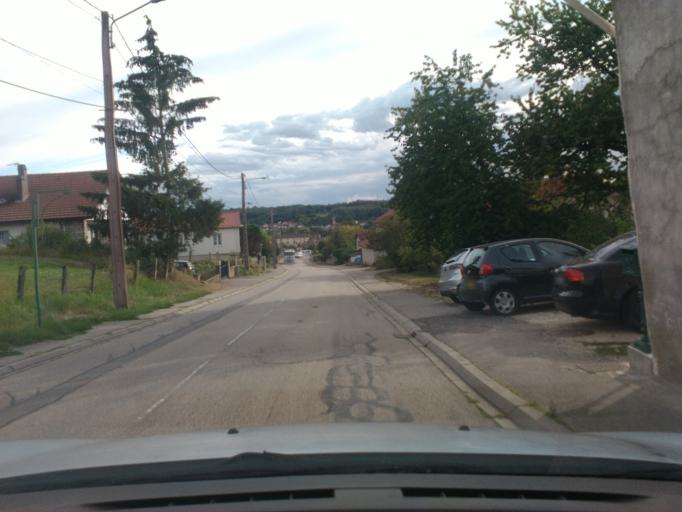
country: FR
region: Lorraine
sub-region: Departement des Vosges
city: Chatel-sur-Moselle
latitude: 48.3154
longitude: 6.3970
